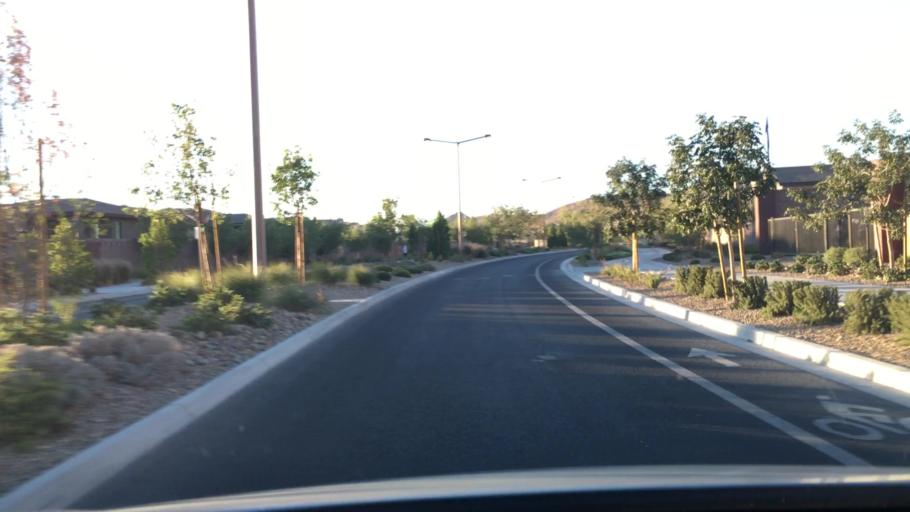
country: US
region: Nevada
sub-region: Clark County
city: Summerlin South
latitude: 36.0768
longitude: -115.3193
